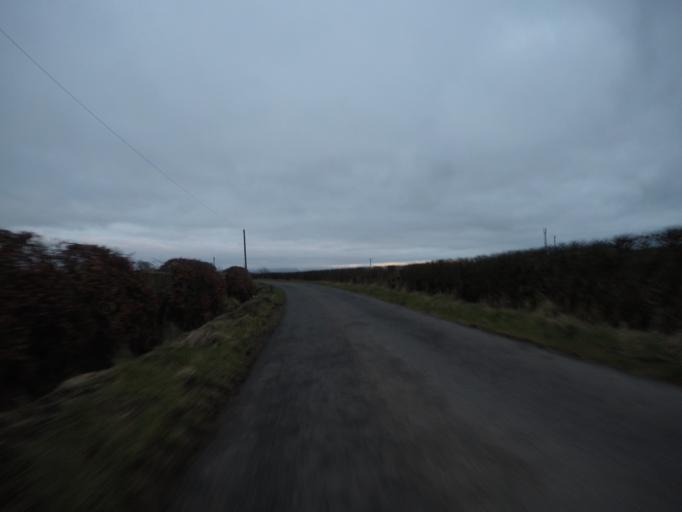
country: GB
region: Scotland
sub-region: North Ayrshire
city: Dalry
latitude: 55.6821
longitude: -4.7282
